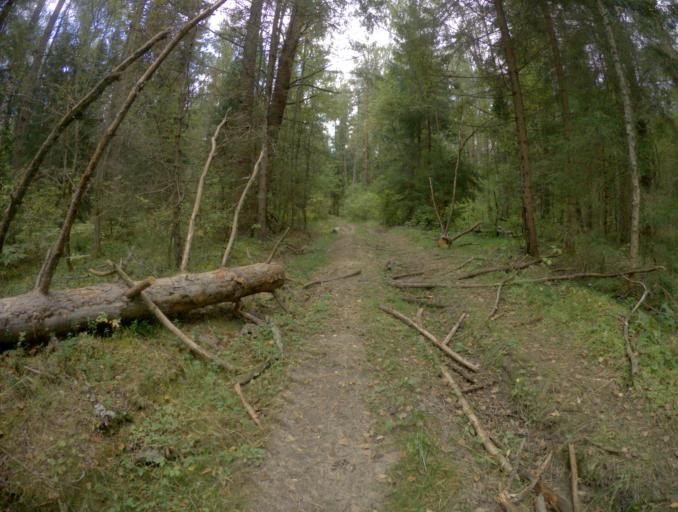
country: RU
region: Vladimir
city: Golovino
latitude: 55.8851
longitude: 40.4356
